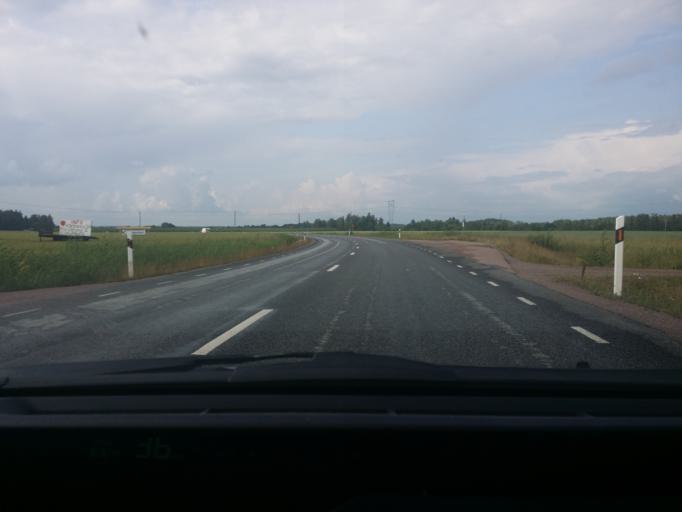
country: SE
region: Vaestmanland
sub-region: Hallstahammars Kommun
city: Kolback
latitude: 59.5667
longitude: 16.2210
